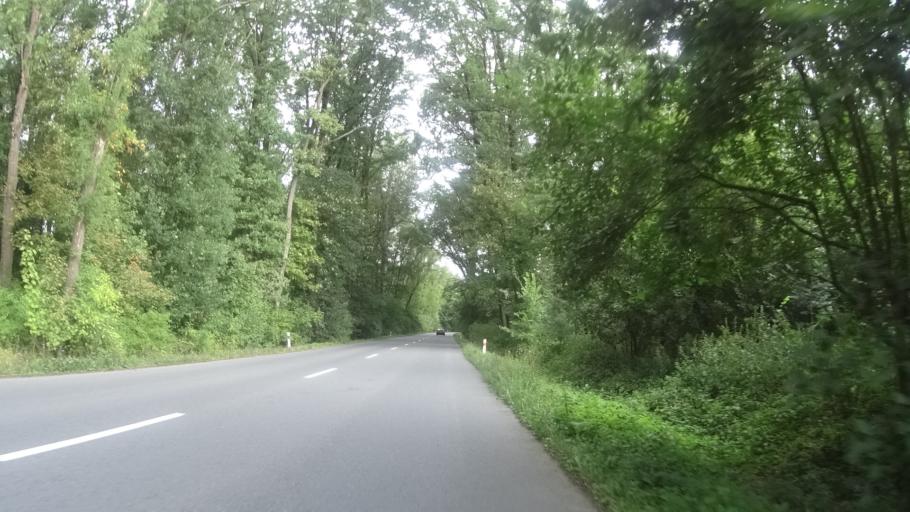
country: CZ
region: Zlin
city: Chropyne
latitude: 49.3306
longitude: 17.3858
